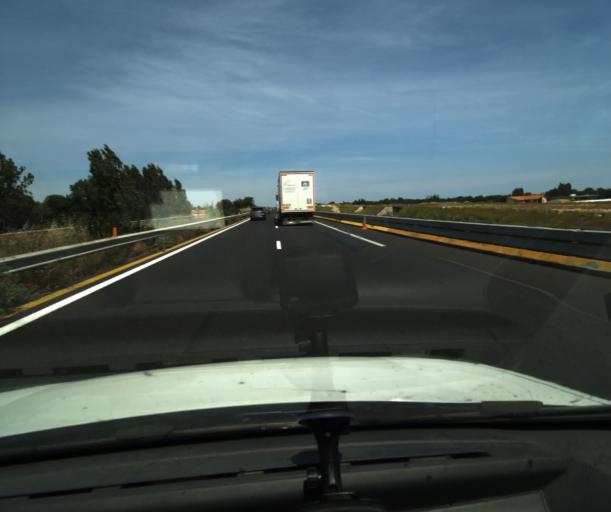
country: FR
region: Languedoc-Roussillon
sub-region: Departement des Pyrenees-Orientales
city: Saint-Esteve
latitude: 42.7086
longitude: 2.8680
